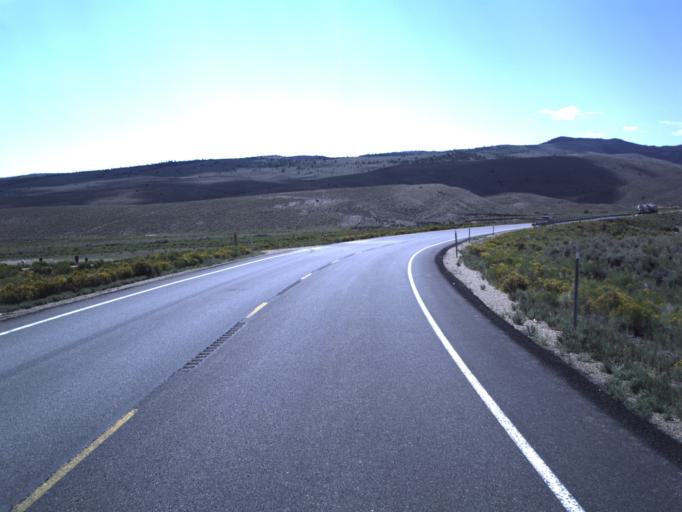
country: US
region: Utah
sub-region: Carbon County
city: Helper
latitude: 39.8088
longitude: -110.7789
